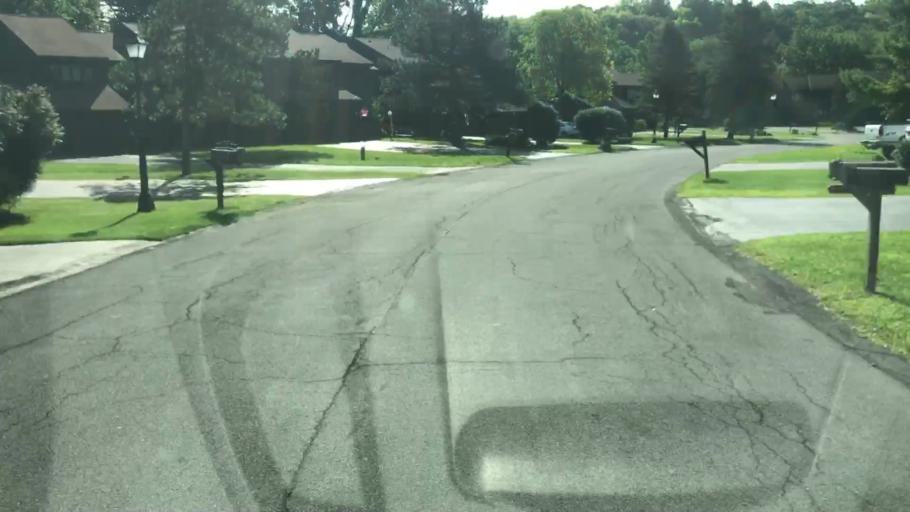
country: US
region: New York
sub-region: Onondaga County
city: Manlius
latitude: 42.9930
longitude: -75.9919
